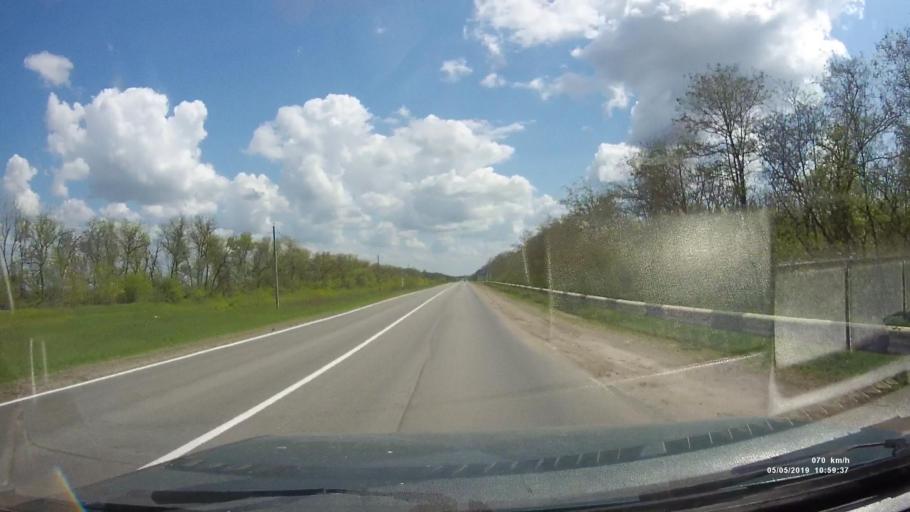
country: RU
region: Rostov
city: Ust'-Donetskiy
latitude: 47.6711
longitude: 40.8717
